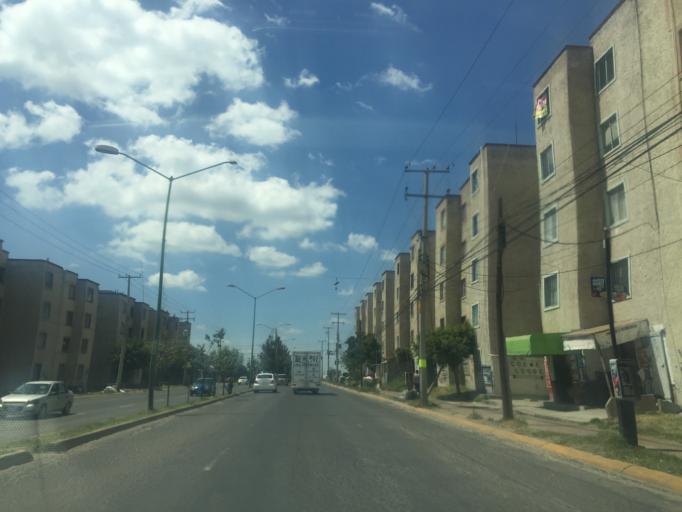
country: MX
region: Guanajuato
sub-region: Leon
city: Ejido la Joya
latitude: 21.1272
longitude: -101.7185
